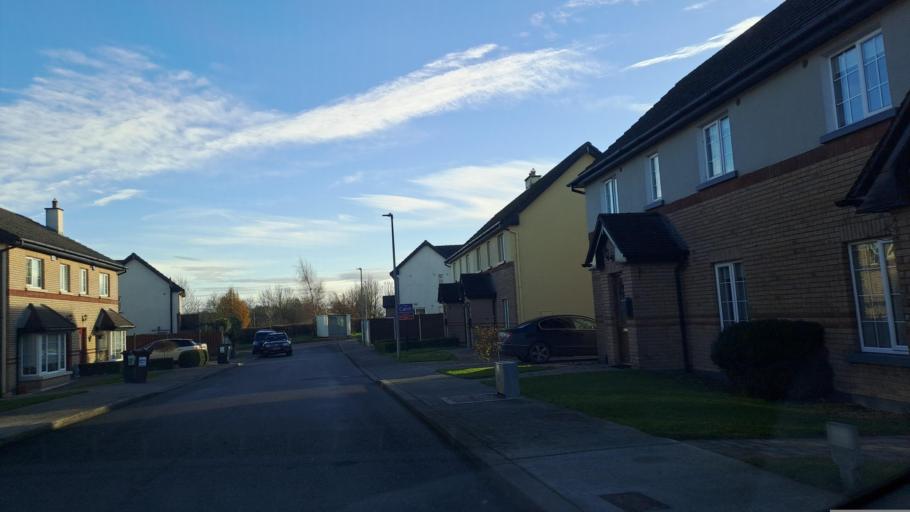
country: IE
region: Ulster
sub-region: An Cabhan
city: Mullagh
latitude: 53.8135
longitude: -6.9458
